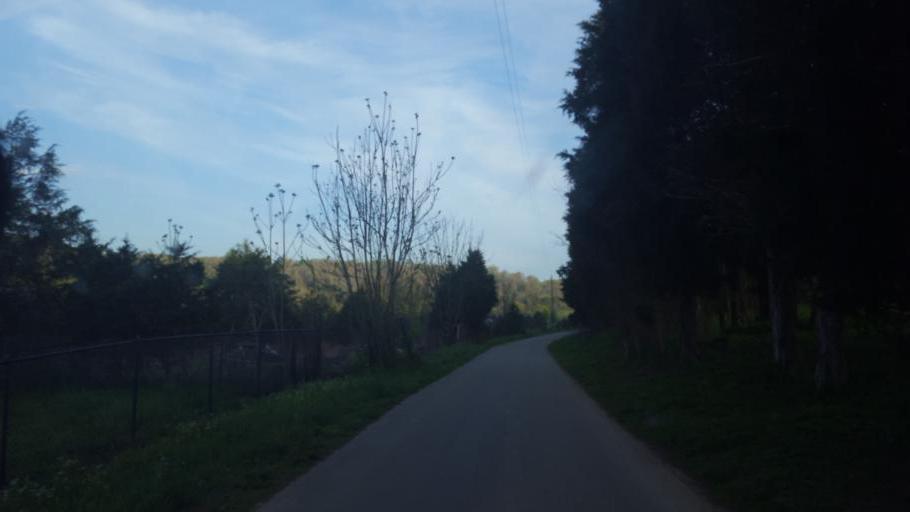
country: US
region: Kentucky
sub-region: Barren County
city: Cave City
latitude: 37.1780
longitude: -86.0056
